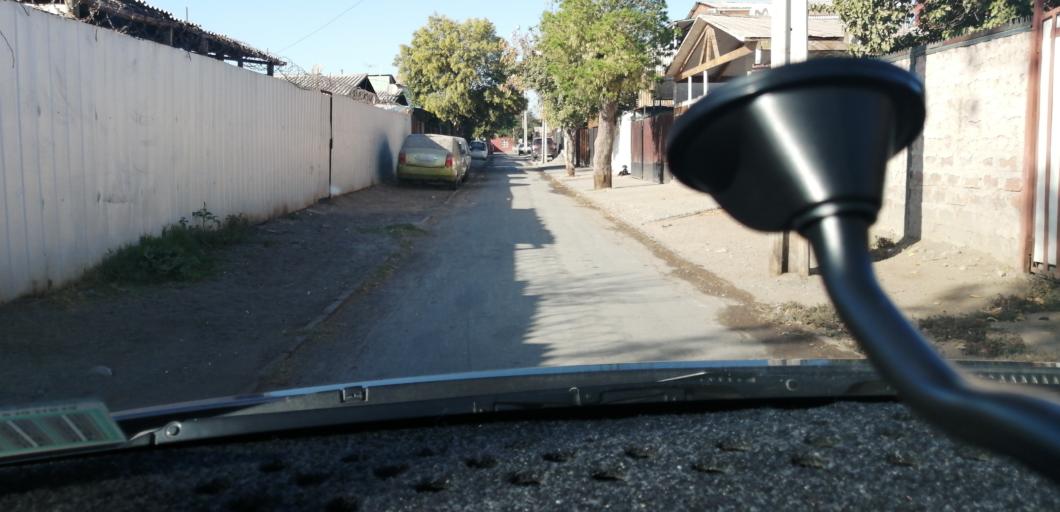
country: CL
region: Santiago Metropolitan
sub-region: Provincia de Santiago
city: Lo Prado
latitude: -33.4272
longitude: -70.7668
